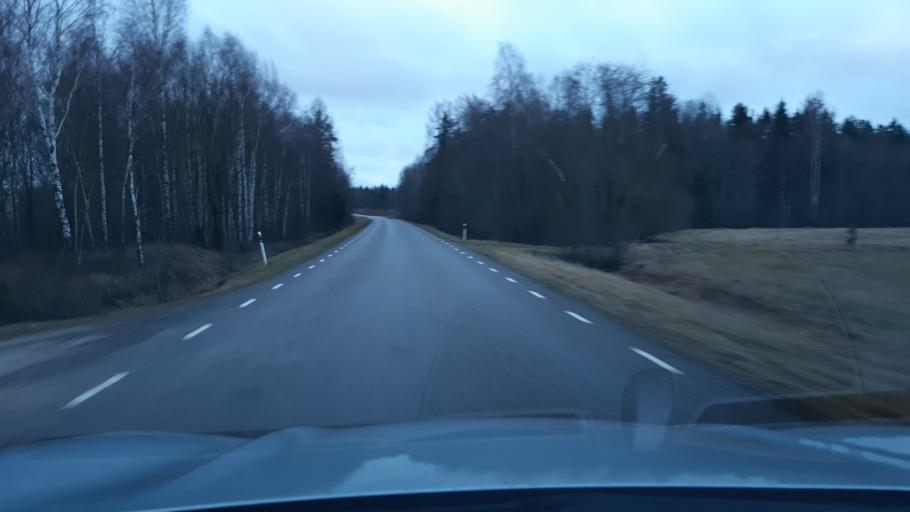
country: EE
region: Raplamaa
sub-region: Kohila vald
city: Kohila
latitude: 59.0860
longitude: 24.6747
